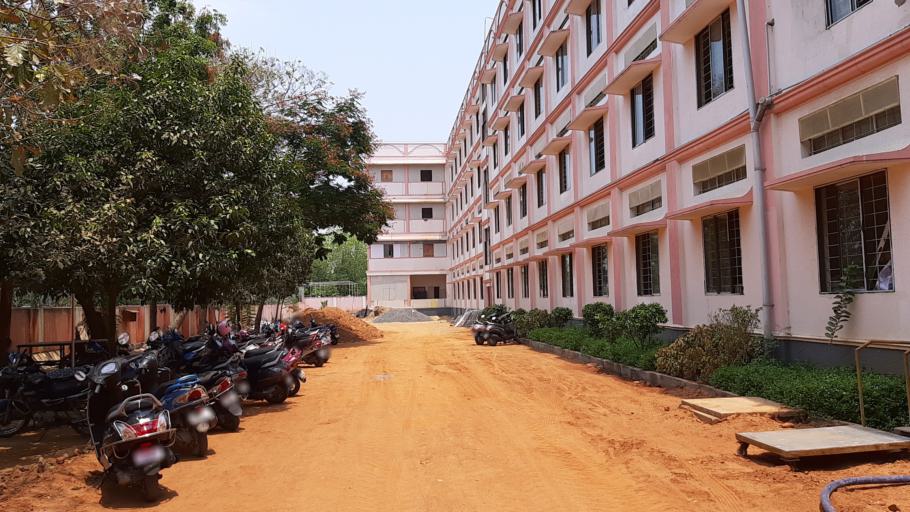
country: IN
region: Tamil Nadu
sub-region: Kancheepuram
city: Saint Thomas Mount
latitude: 13.0236
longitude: 80.1892
